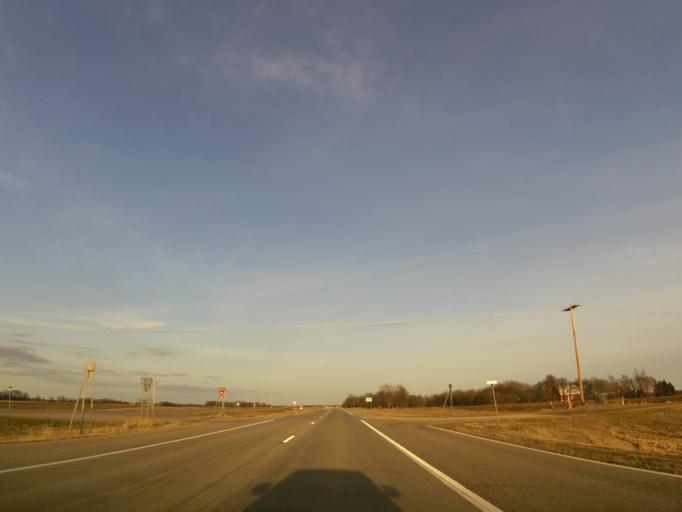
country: US
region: Minnesota
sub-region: Carver County
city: Norwood (historical)
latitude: 44.7679
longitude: -94.0110
